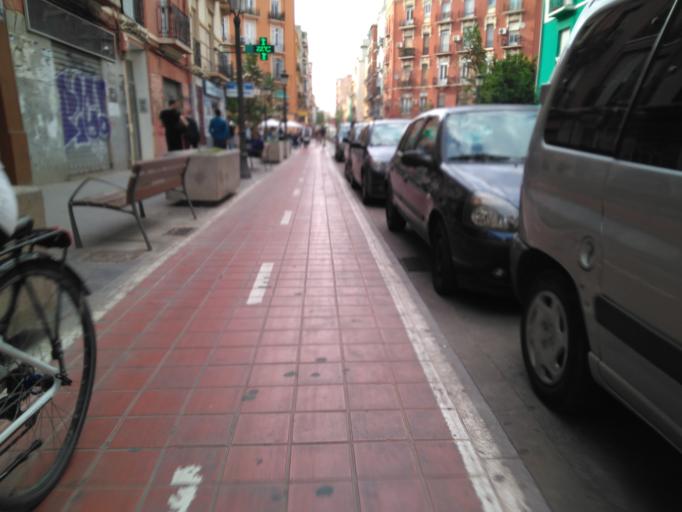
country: ES
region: Valencia
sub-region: Provincia de Valencia
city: Valencia
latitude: 39.4606
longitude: -0.3761
